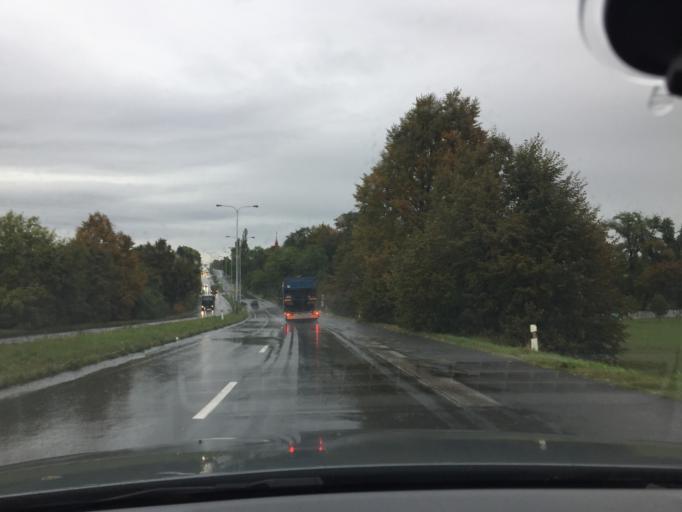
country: CZ
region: Central Bohemia
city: Zdiby
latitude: 50.1643
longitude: 14.4530
